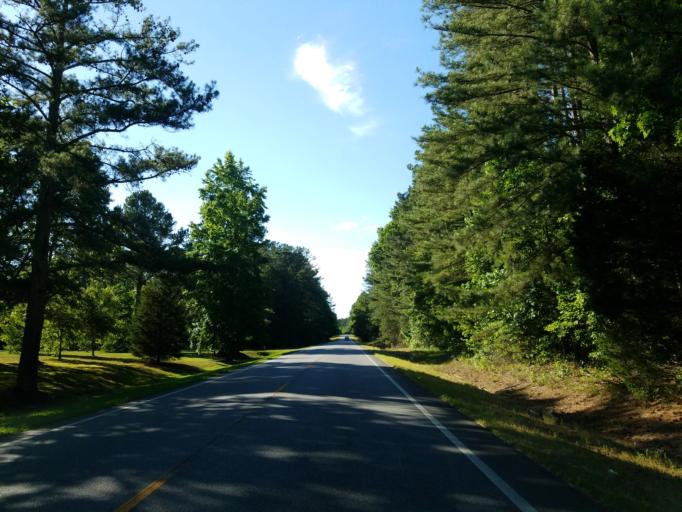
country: US
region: Georgia
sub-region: Gordon County
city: Calhoun
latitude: 34.6012
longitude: -85.0364
